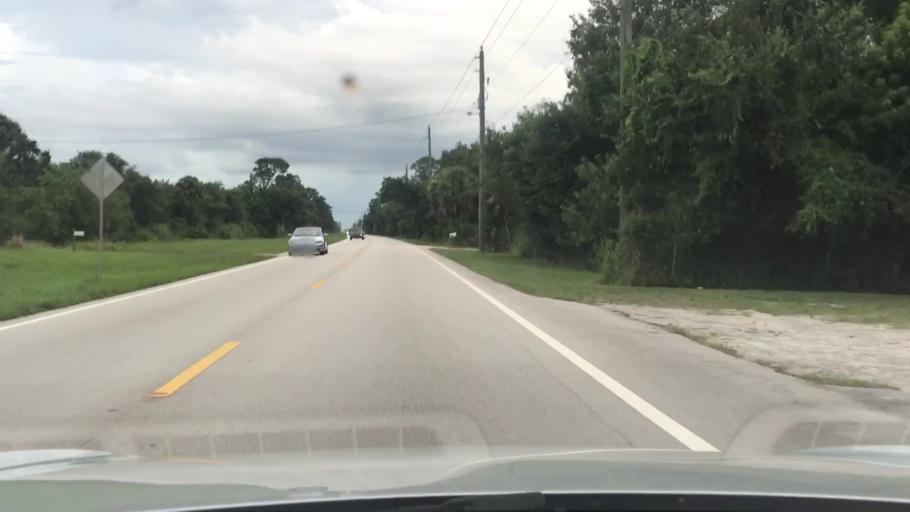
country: US
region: Florida
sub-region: Indian River County
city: Winter Beach
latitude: 27.7317
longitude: -80.4623
